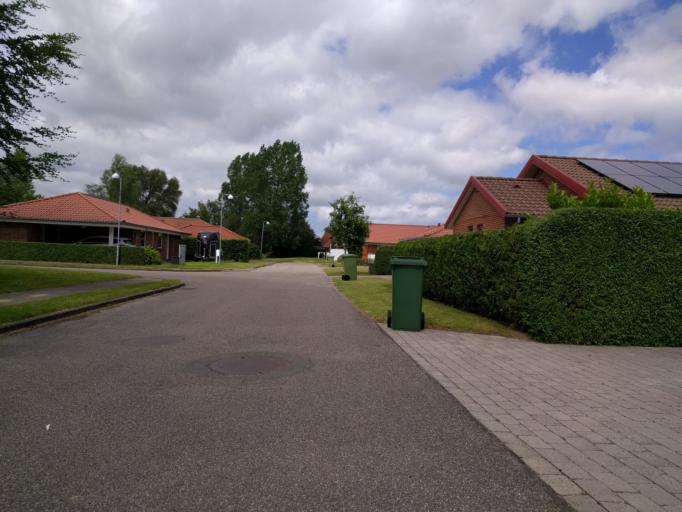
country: DK
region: South Denmark
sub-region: Odense Kommune
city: Bullerup
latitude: 55.4257
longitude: 10.4671
